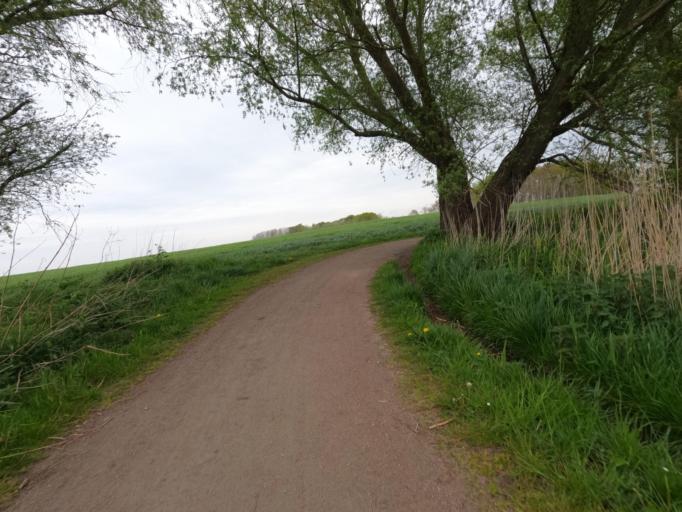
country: DE
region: Mecklenburg-Vorpommern
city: Ostseebad Dierhagen
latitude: 54.2778
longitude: 12.3760
